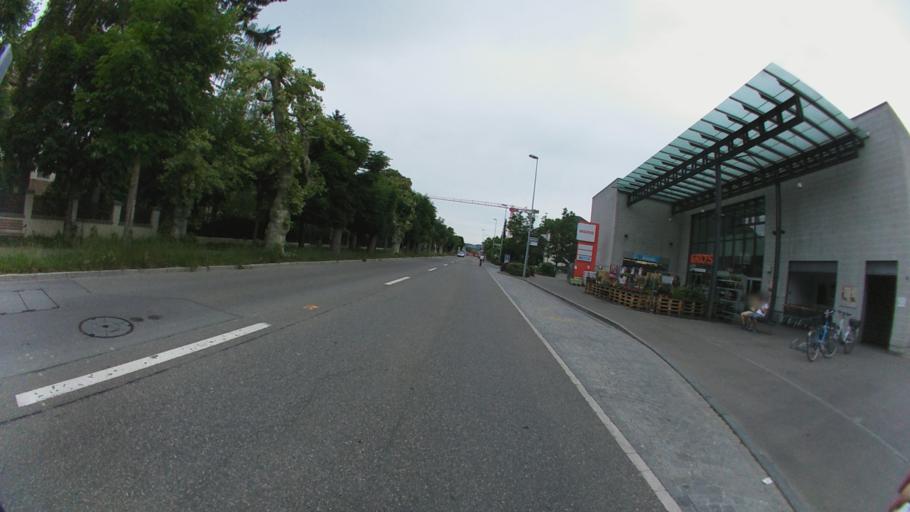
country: CH
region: Aargau
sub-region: Bezirk Zurzach
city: Bad Zurzach
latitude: 47.5864
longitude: 8.2958
